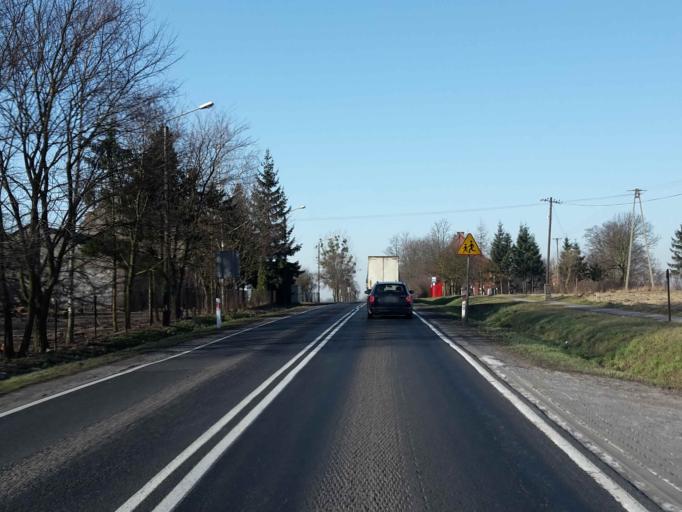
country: PL
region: Kujawsko-Pomorskie
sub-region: Powiat inowroclawski
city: Gniewkowo
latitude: 52.9104
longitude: 18.4768
